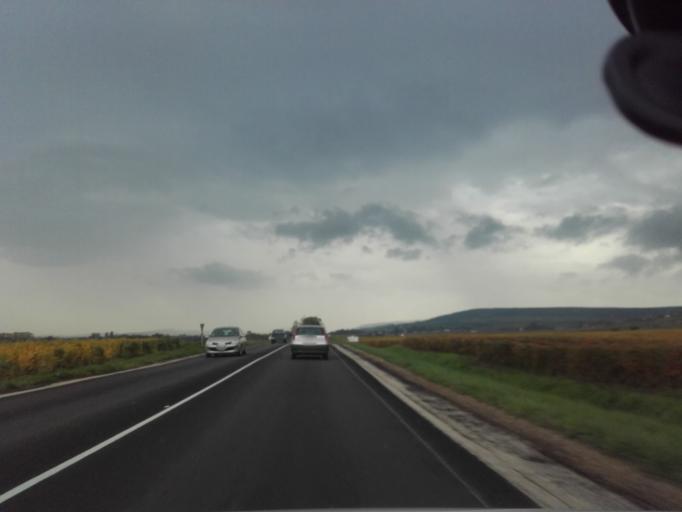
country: FR
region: Bourgogne
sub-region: Departement de la Cote-d'Or
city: Bligny-les-Beaune
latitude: 46.9973
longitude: 4.7971
